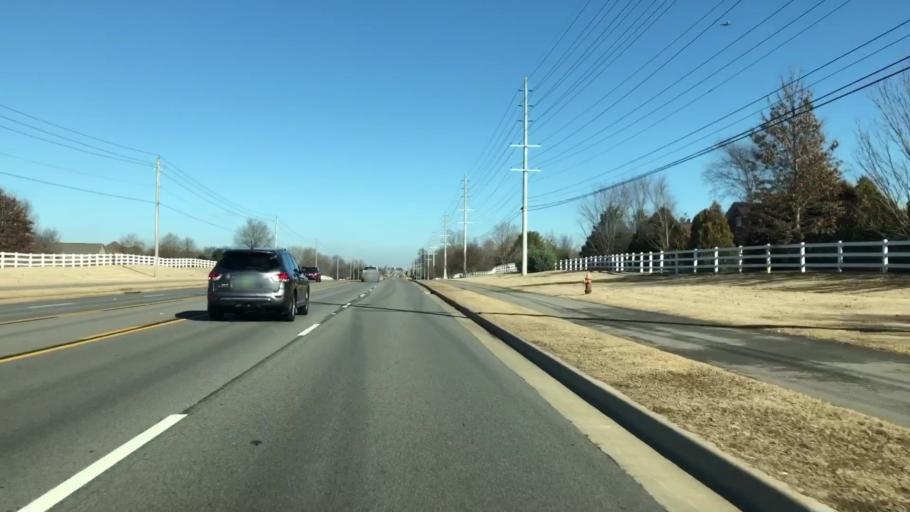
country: US
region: Alabama
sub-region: Madison County
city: Madison
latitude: 34.7103
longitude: -86.7864
